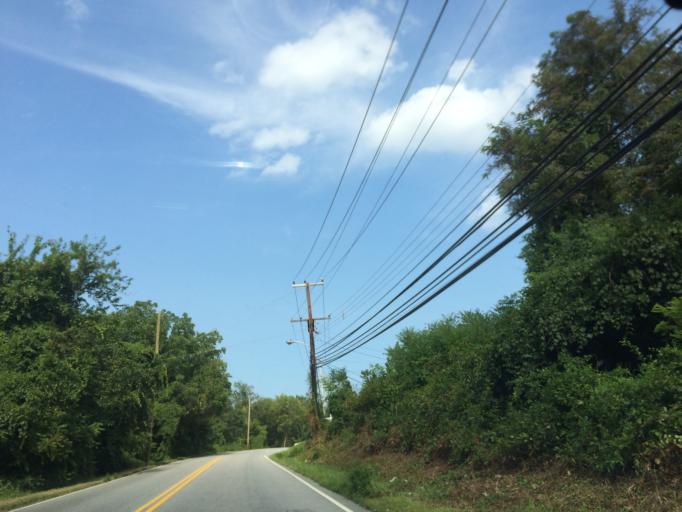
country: US
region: Maryland
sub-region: Baltimore County
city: Lansdowne
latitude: 39.2224
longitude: -76.6728
